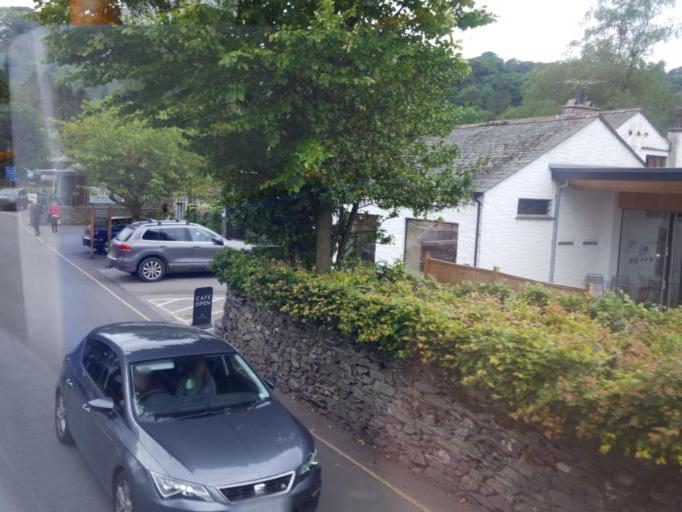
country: GB
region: England
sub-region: Cumbria
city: Ambleside
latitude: 54.4596
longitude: -3.0245
